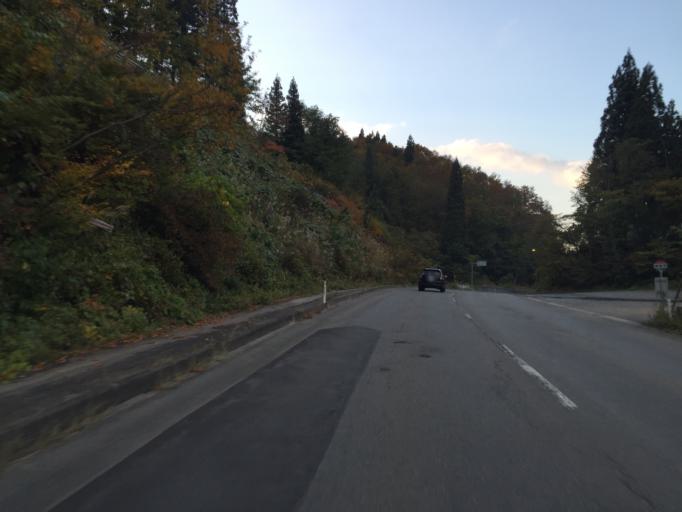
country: JP
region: Yamagata
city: Yonezawa
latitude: 37.8487
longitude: 139.9949
